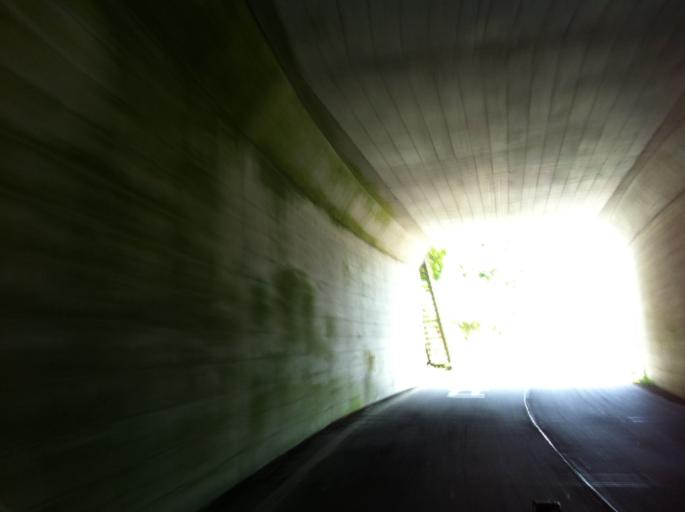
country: JP
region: Shizuoka
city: Shizuoka-shi
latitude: 35.1875
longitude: 138.3616
